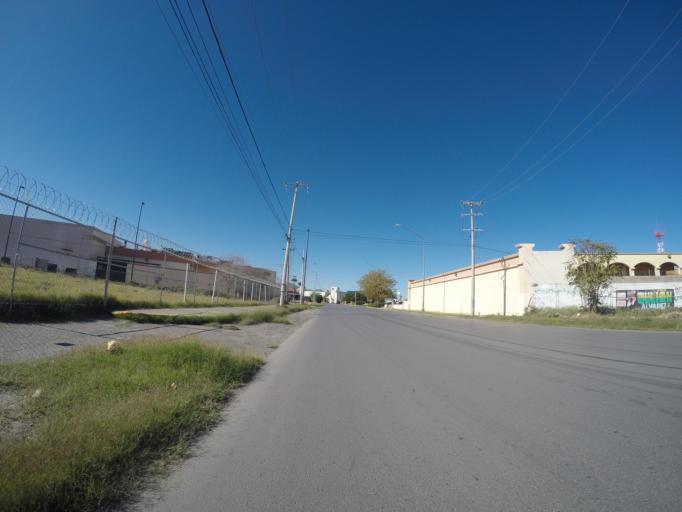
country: MX
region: Chihuahua
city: Ciudad Juarez
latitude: 31.7427
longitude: -106.4510
